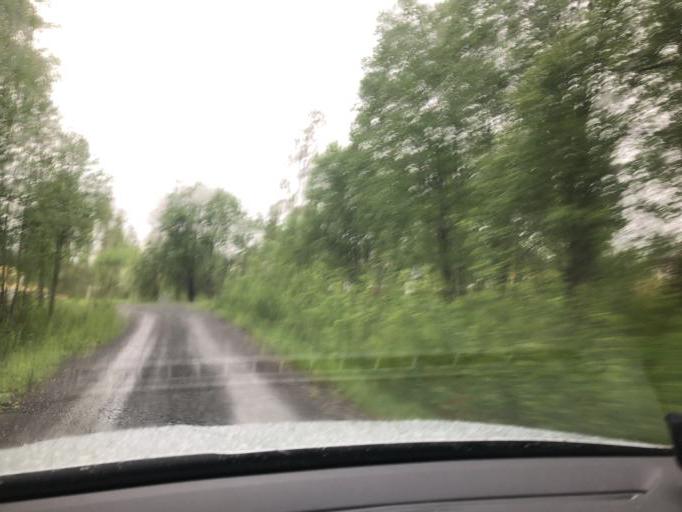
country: SE
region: Vaesternorrland
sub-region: Haernoesands Kommun
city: Haernoesand
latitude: 62.7936
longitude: 17.9253
